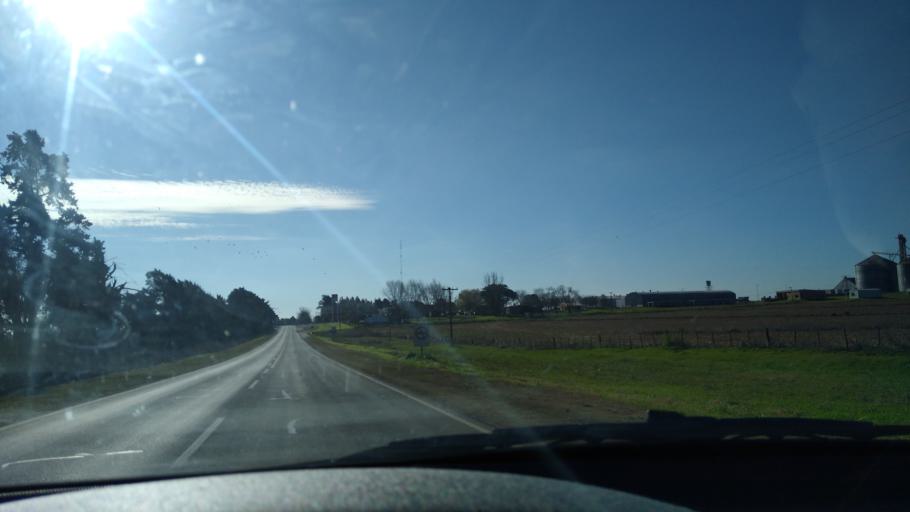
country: AR
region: Entre Rios
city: Aranguren
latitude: -32.4251
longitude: -60.3120
